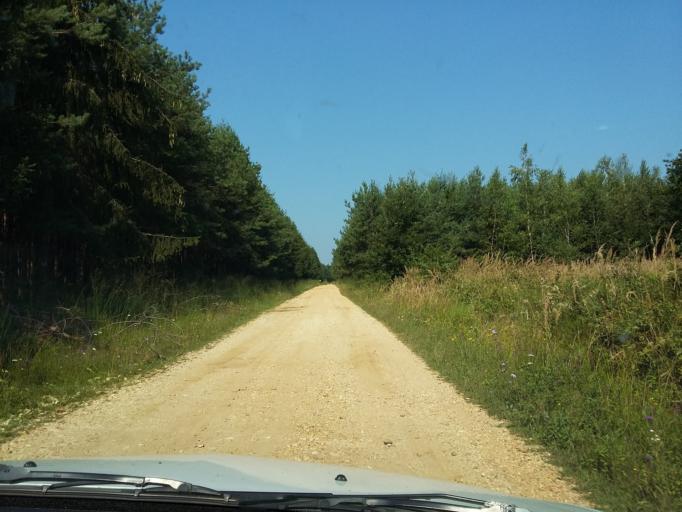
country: SI
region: Hodos-Hodos
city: Hodos
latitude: 46.8570
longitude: 16.3214
